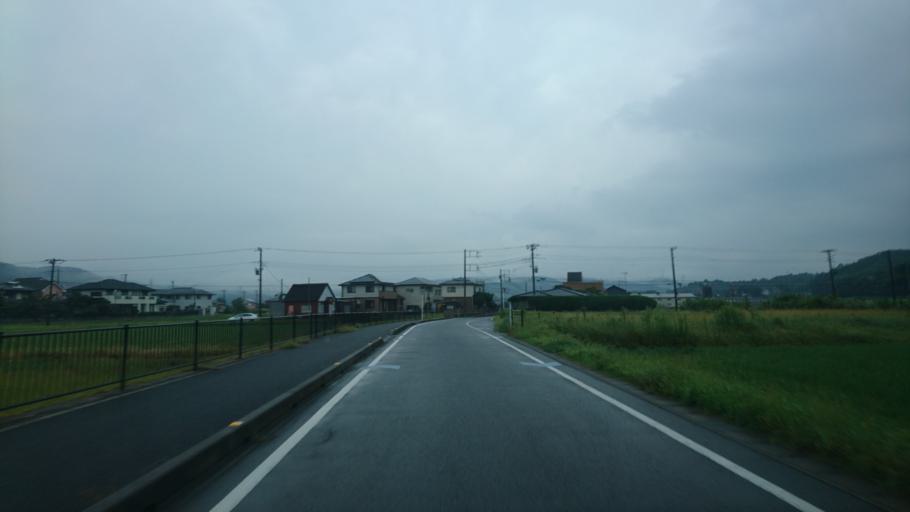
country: JP
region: Chiba
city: Kimitsu
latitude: 35.3033
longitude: 139.9661
